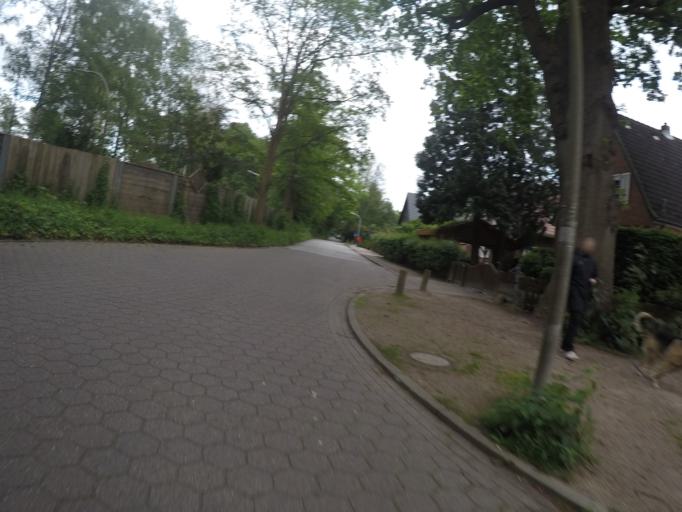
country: DE
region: Schleswig-Holstein
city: Bonningstedt
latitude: 53.6440
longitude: 9.9253
